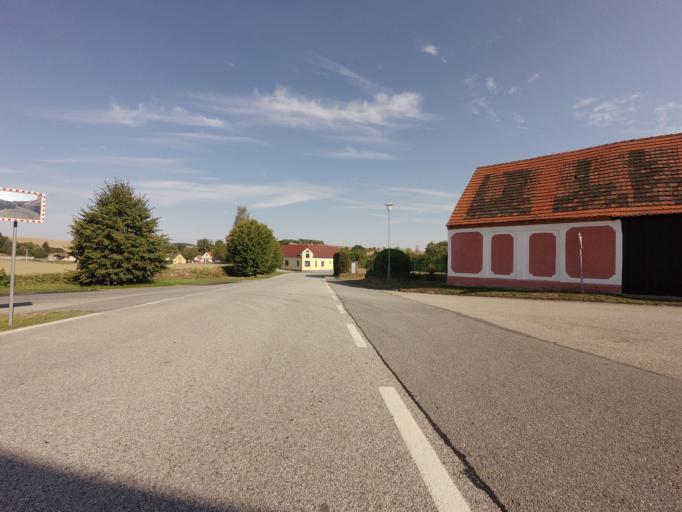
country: CZ
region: Jihocesky
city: Tyn nad Vltavou
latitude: 49.2783
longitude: 14.3987
